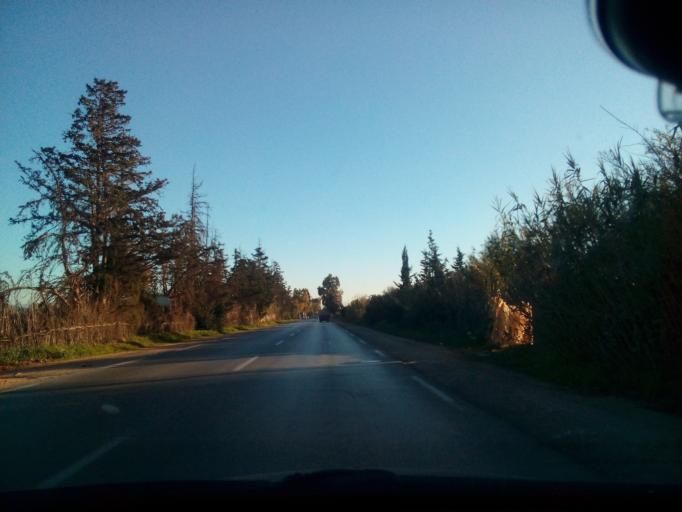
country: DZ
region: Mostaganem
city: Mostaganem
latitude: 35.8045
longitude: 0.1717
